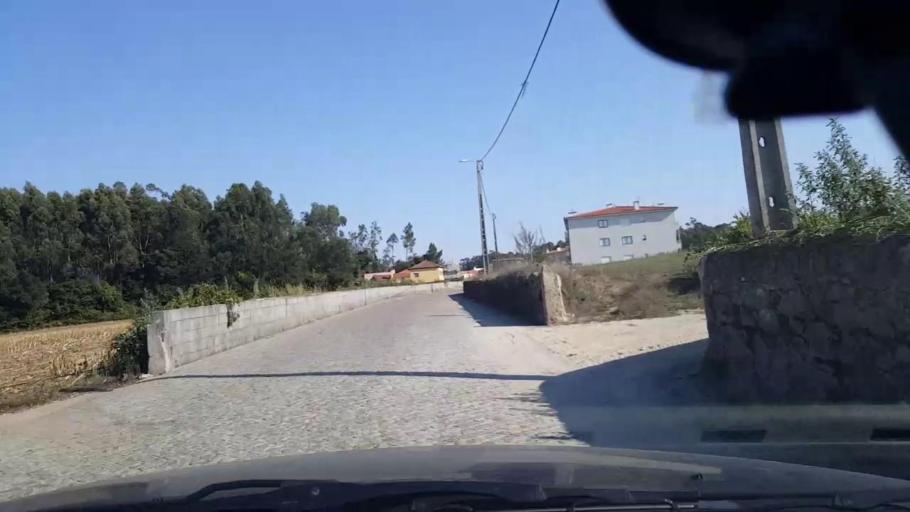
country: PT
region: Porto
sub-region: Vila do Conde
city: Arvore
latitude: 41.3585
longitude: -8.7071
